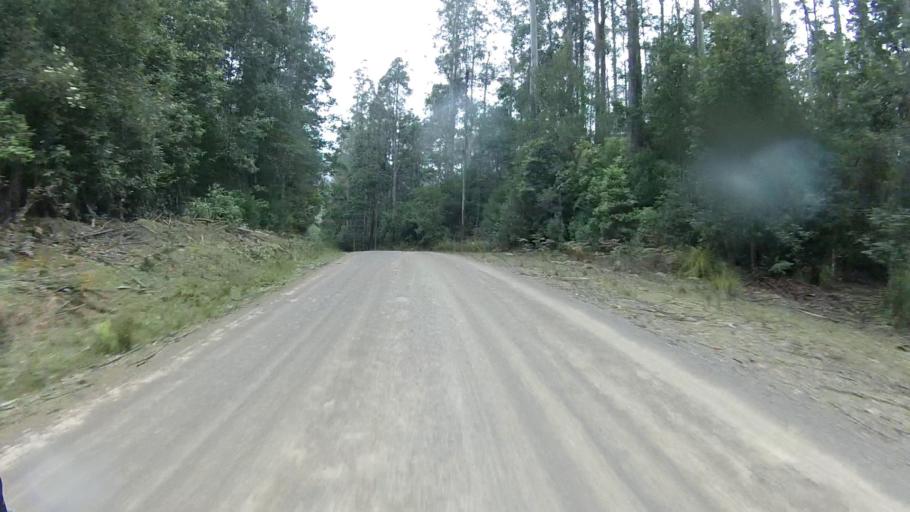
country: AU
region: Tasmania
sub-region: Sorell
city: Sorell
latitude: -42.7092
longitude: 147.8401
